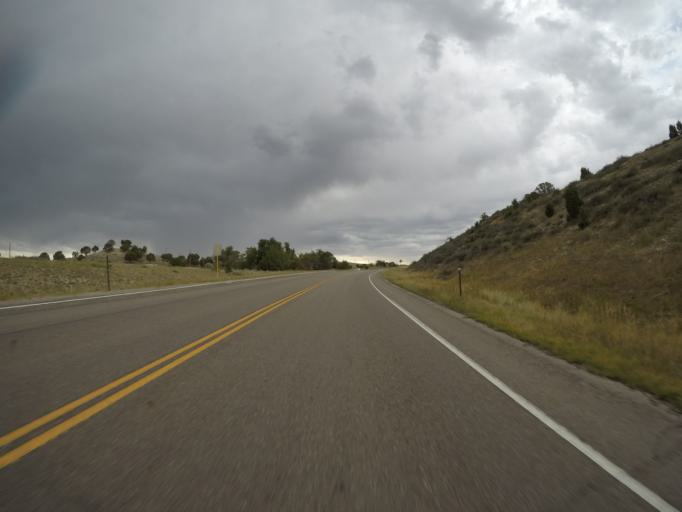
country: US
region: Colorado
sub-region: Rio Blanco County
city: Rangely
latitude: 40.3545
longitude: -108.4504
